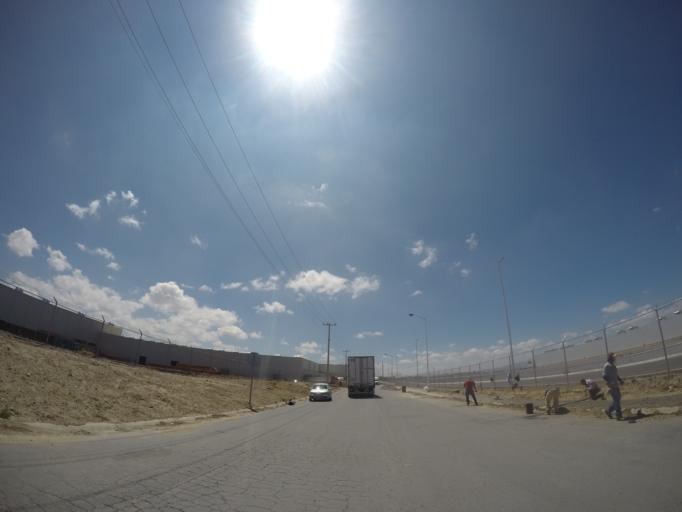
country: MX
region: San Luis Potosi
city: La Pila
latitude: 21.9758
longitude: -100.8795
